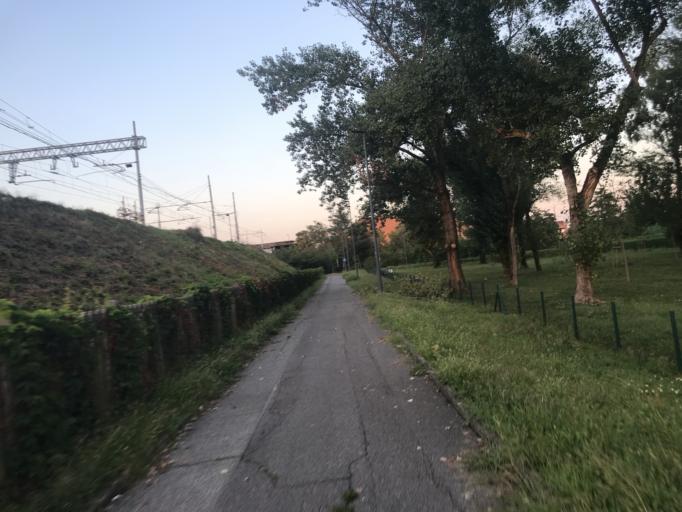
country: IT
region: Lombardy
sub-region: Citta metropolitana di Milano
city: Cologno Monzese
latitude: 45.5104
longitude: 9.2571
